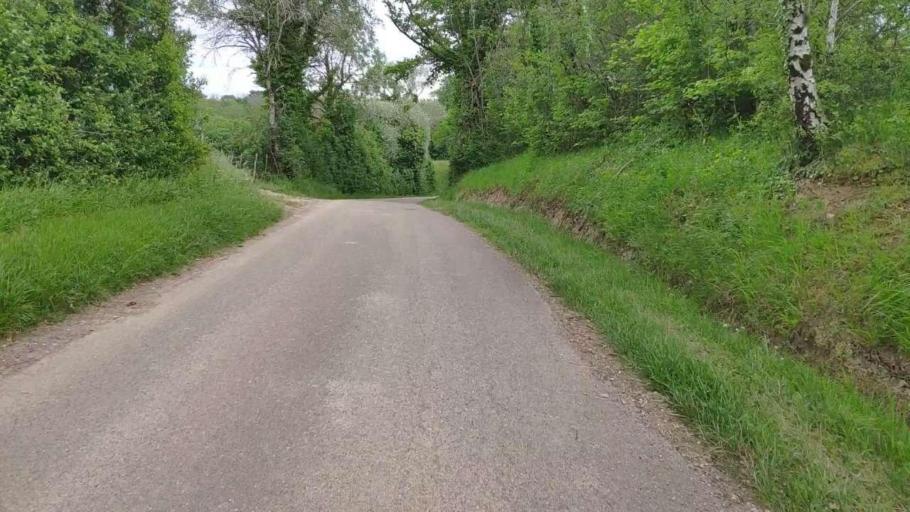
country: FR
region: Franche-Comte
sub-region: Departement du Jura
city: Montmorot
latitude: 46.7482
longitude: 5.5276
